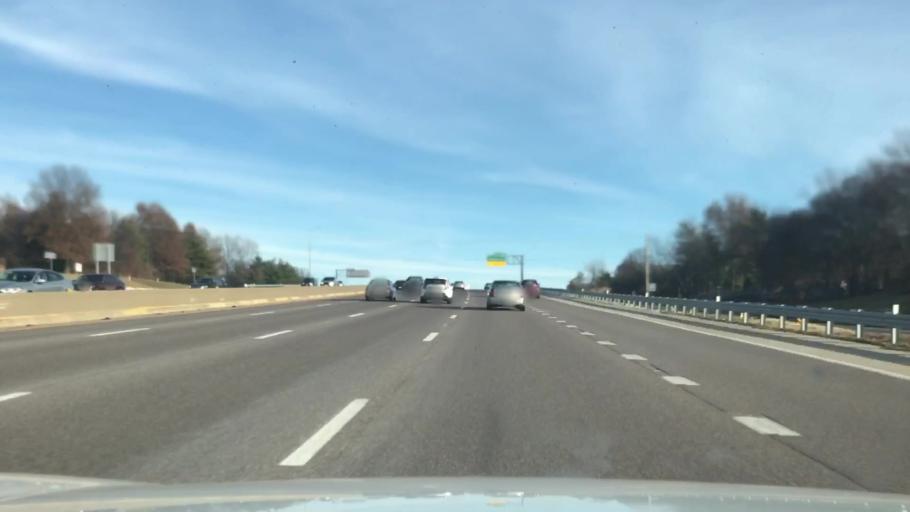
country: US
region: Missouri
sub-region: Saint Louis County
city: Town and Country
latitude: 38.6400
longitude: -90.4963
